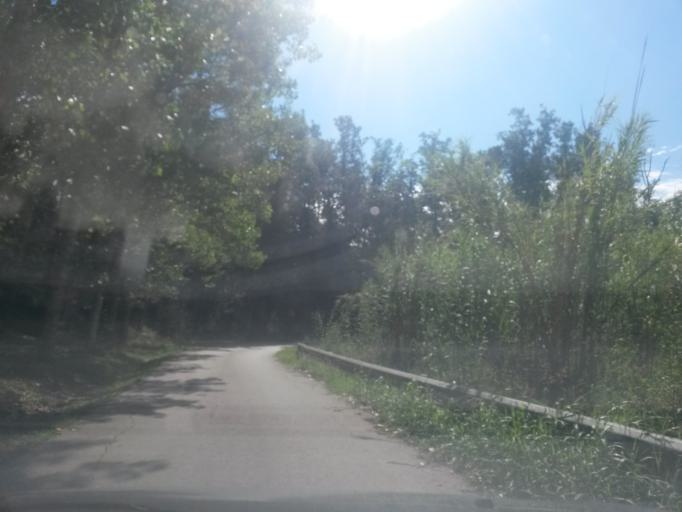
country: ES
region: Catalonia
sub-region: Provincia de Girona
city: la Cellera de Ter
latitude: 41.9772
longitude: 2.6221
